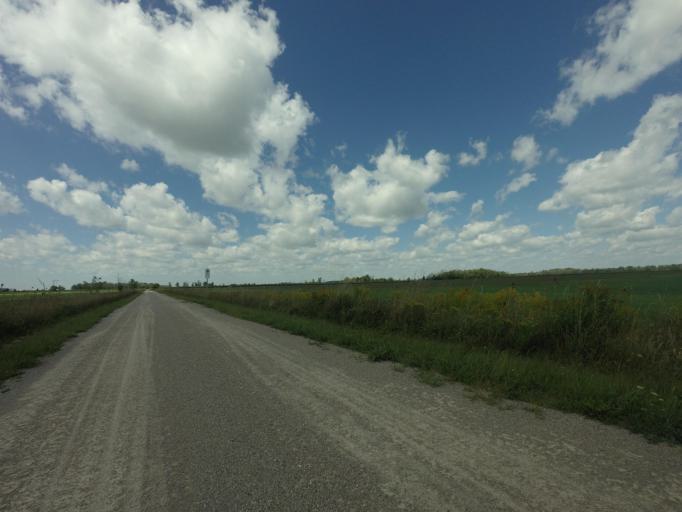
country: CA
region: Ontario
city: Huron East
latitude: 43.6078
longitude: -81.1244
